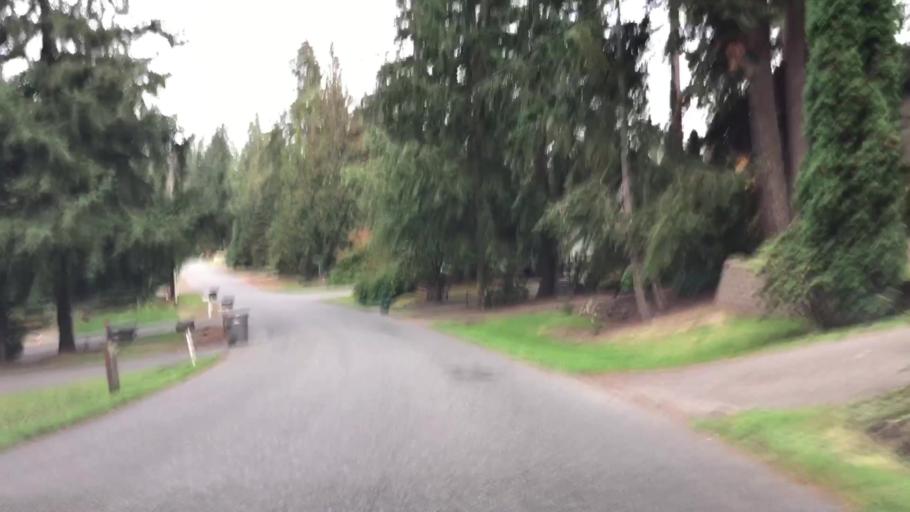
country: US
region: Washington
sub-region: King County
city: Cottage Lake
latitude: 47.7424
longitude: -122.0962
